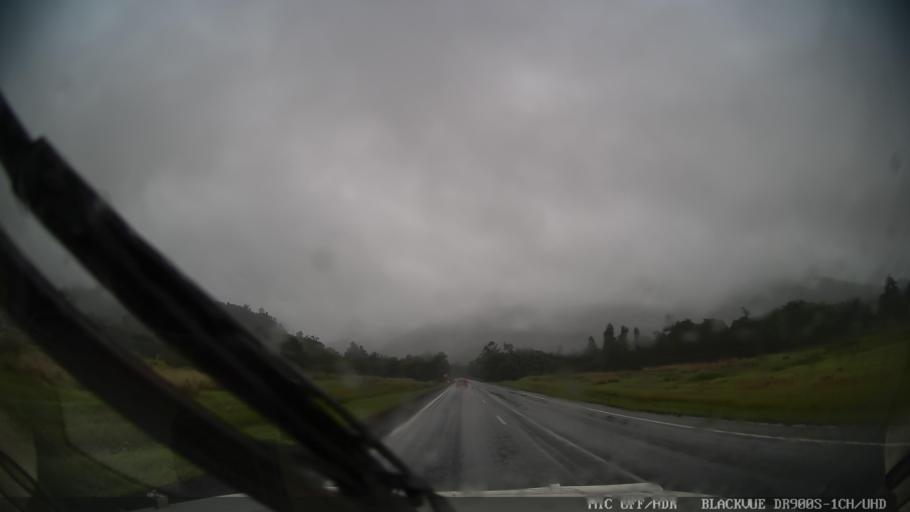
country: AU
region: Queensland
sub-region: Cassowary Coast
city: Innisfail
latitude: -17.8653
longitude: 145.9821
